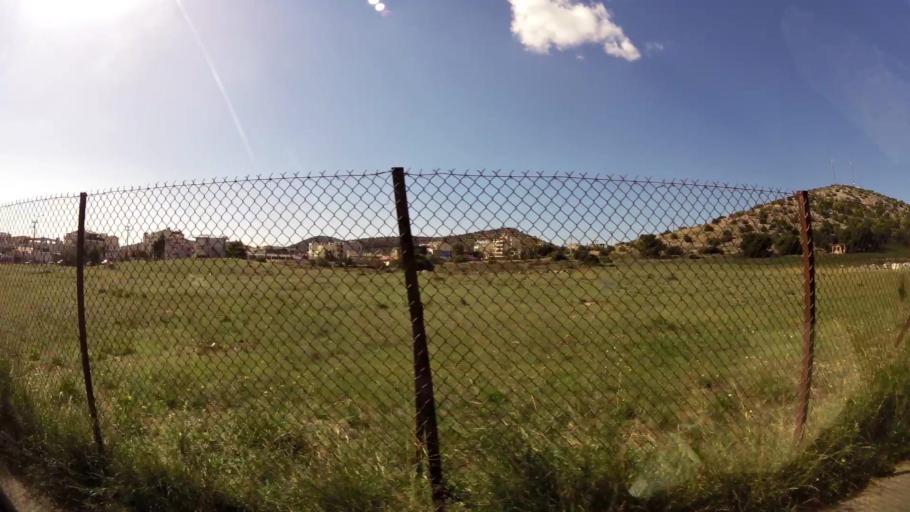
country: GR
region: Attica
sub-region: Nomarchia Anatolikis Attikis
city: Vari
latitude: 37.8359
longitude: 23.8052
